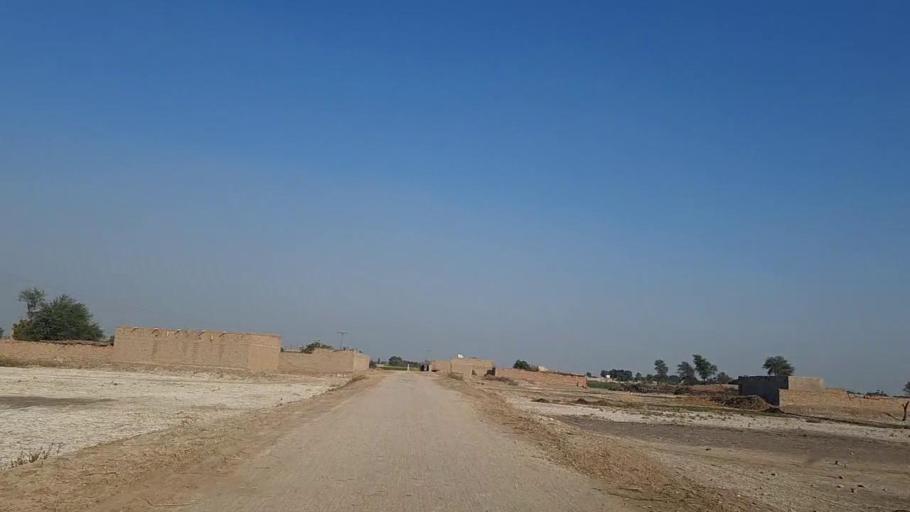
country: PK
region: Sindh
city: Daur
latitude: 26.3172
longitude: 68.1685
